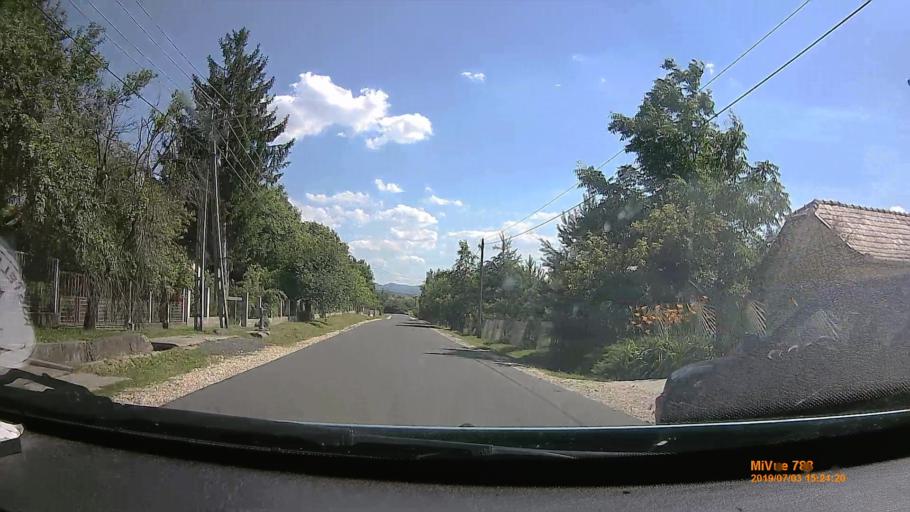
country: HU
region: Borsod-Abauj-Zemplen
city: Farkaslyuk
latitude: 48.1940
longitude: 20.3926
